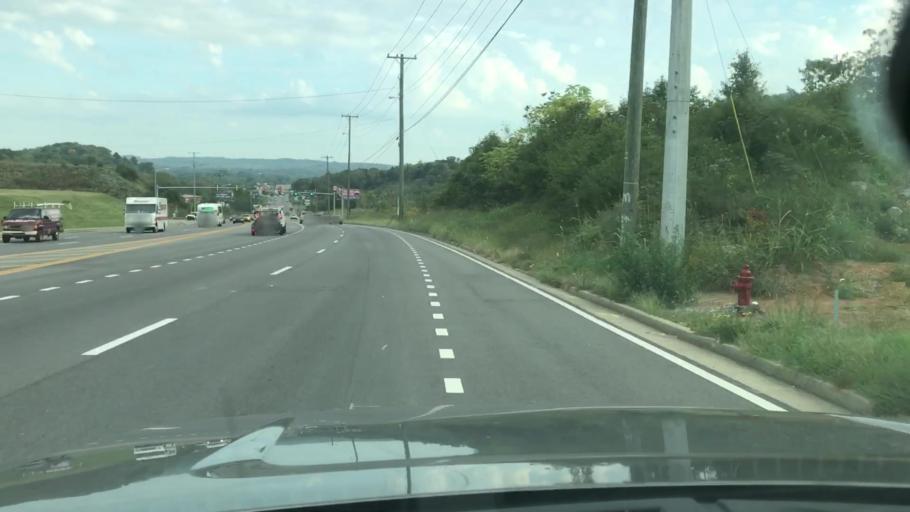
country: US
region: Tennessee
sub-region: Davidson County
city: Nashville
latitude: 36.2449
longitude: -86.7564
